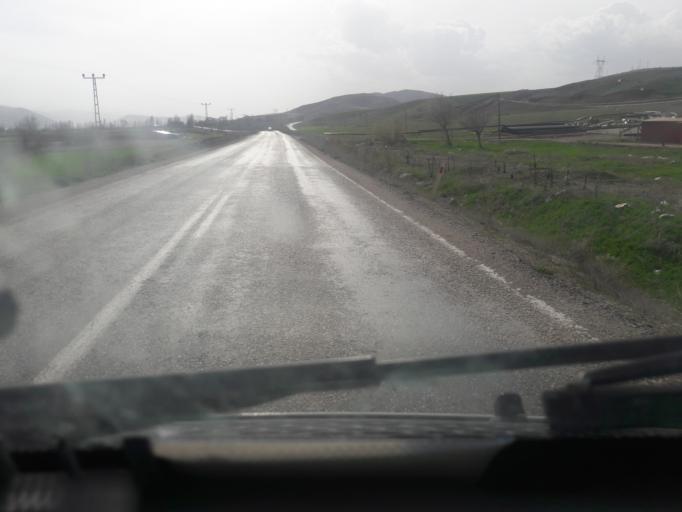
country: TR
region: Gumushane
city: Kelkit
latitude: 40.1430
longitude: 39.4053
